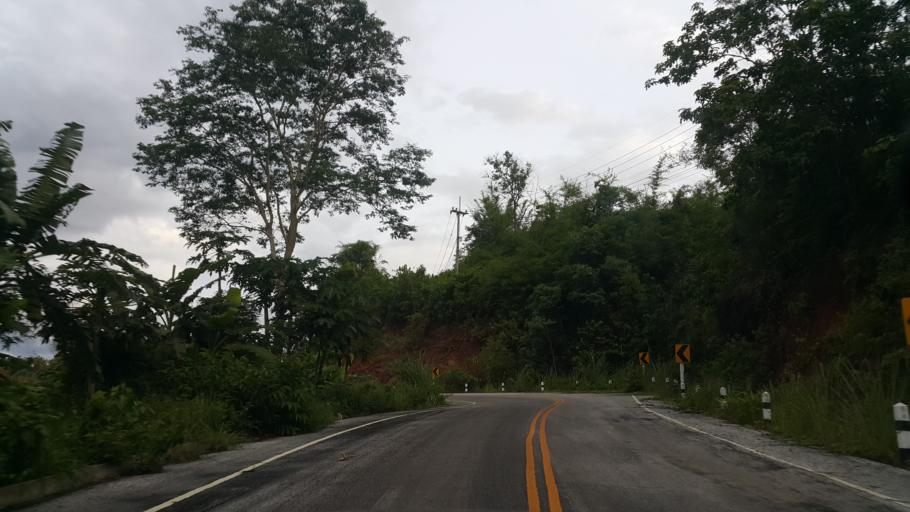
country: TH
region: Loei
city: Na Haeo
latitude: 17.4740
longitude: 101.1144
